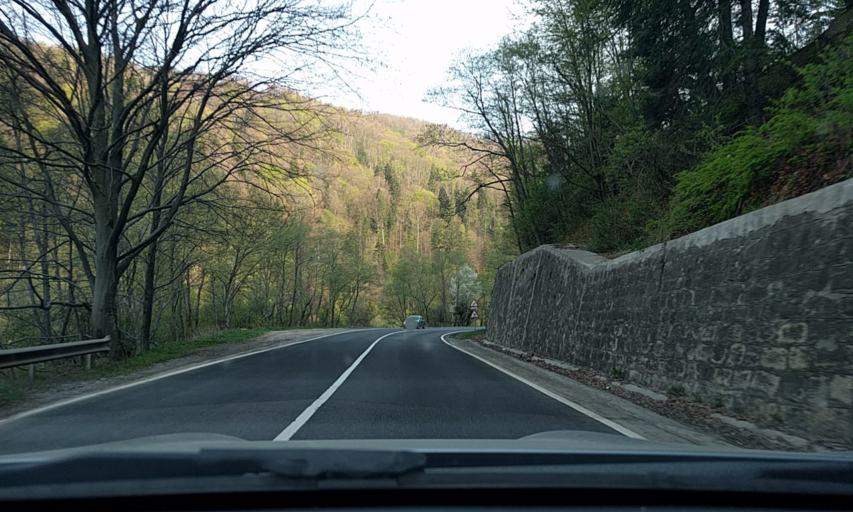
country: RO
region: Covasna
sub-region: Comuna Bretcu
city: Bretcu
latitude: 46.0817
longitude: 26.3976
